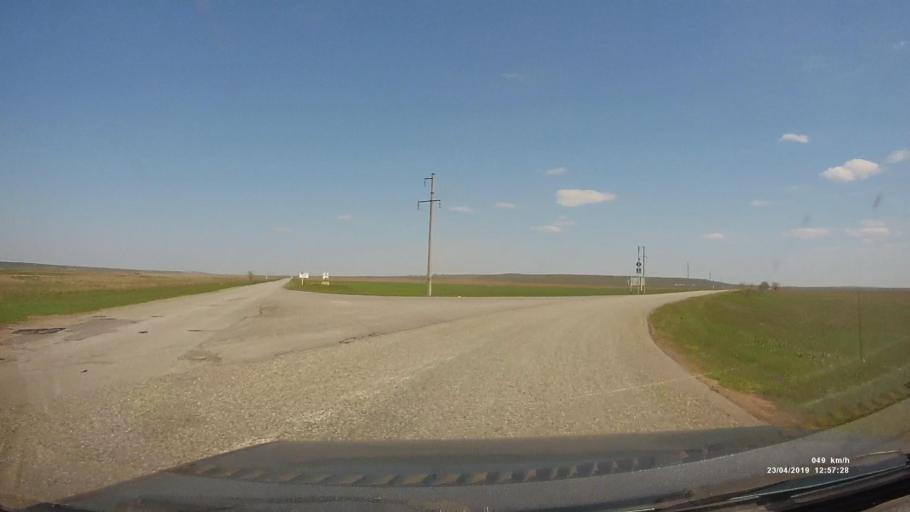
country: RU
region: Kalmykiya
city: Yashalta
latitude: 46.6038
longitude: 42.5815
